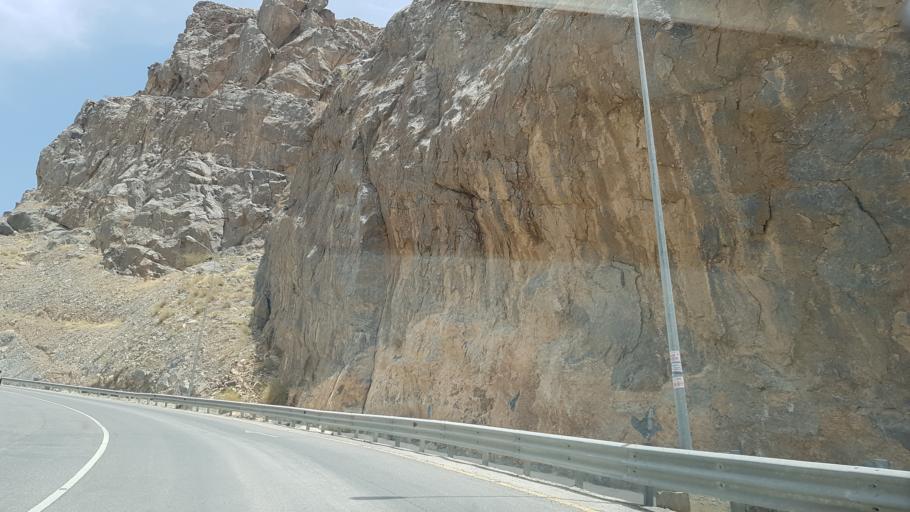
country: OM
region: Muhafazat ad Dakhiliyah
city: Izki
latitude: 22.9551
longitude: 57.6745
